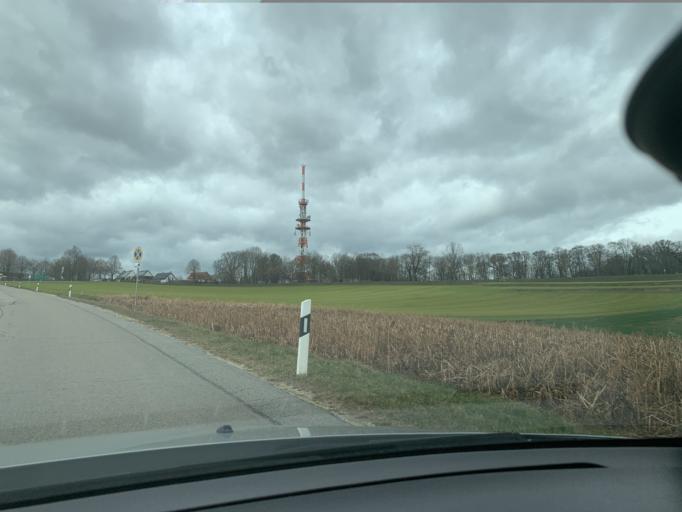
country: DE
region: Bavaria
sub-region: Lower Bavaria
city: Landshut
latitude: 48.5223
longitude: 12.1751
